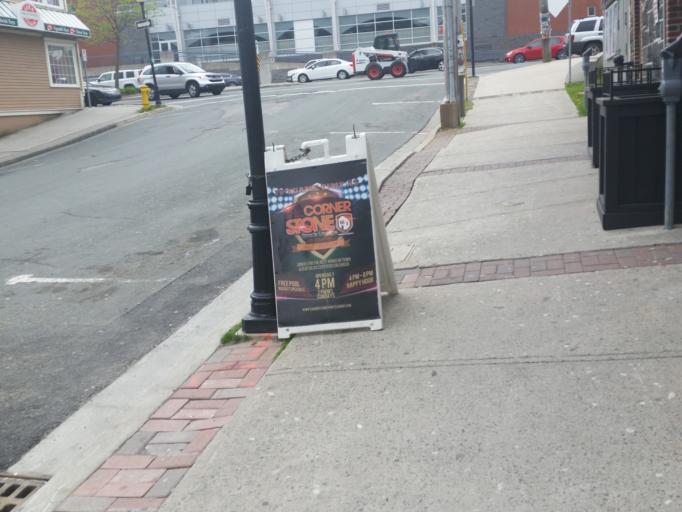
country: CA
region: Newfoundland and Labrador
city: St. John's
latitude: 47.5602
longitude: -52.7120
